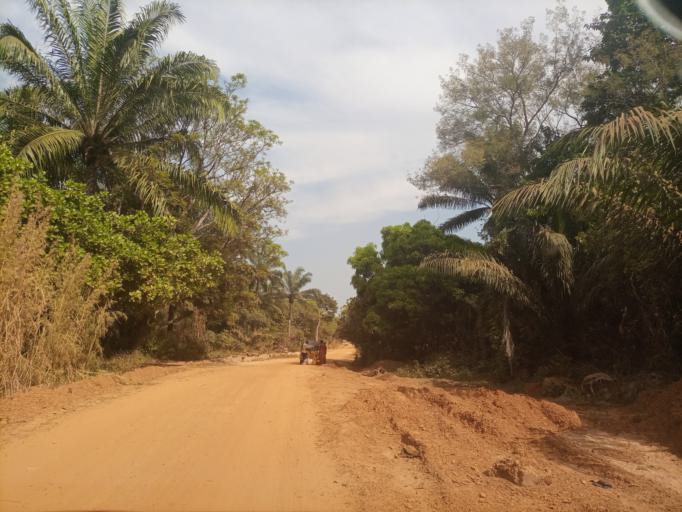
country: NG
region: Enugu
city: Opi
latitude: 6.8103
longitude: 7.5237
